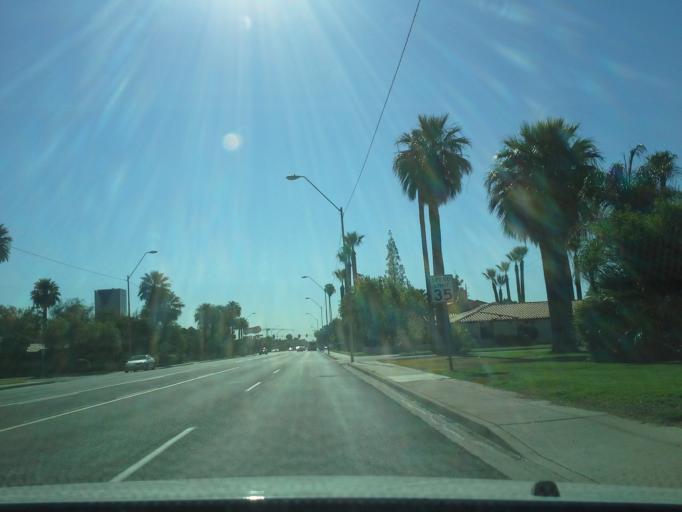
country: US
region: Arizona
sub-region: Maricopa County
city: Phoenix
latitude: 33.4658
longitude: -112.0856
